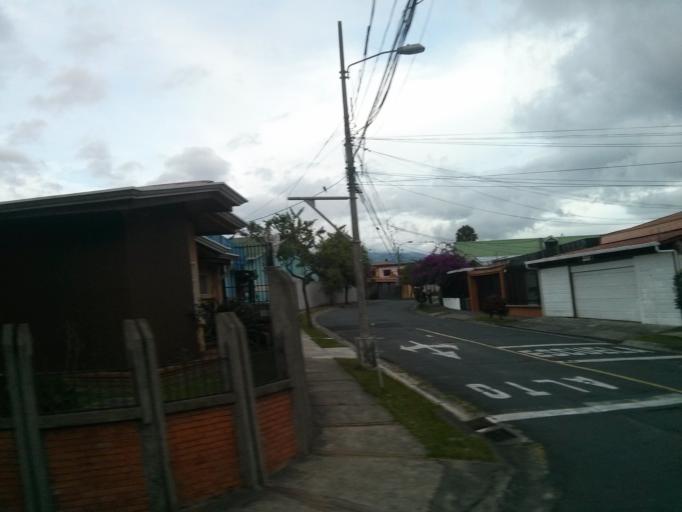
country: CR
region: San Jose
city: San Pedro
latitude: 9.9089
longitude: -84.0608
